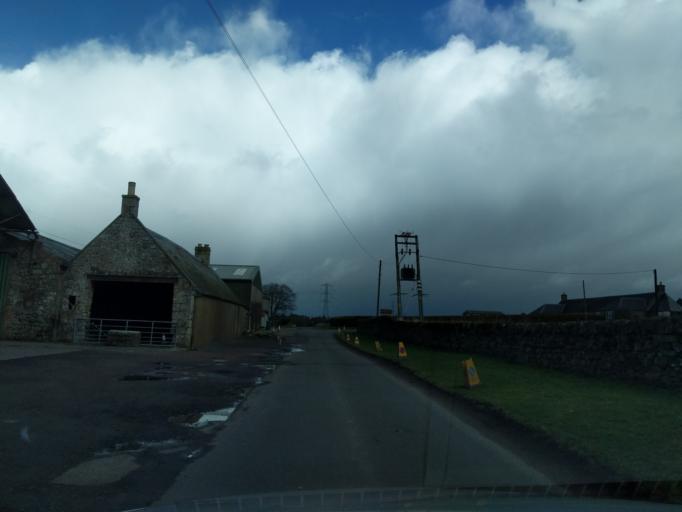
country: GB
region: Scotland
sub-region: Edinburgh
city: Currie
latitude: 55.8768
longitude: -3.3143
